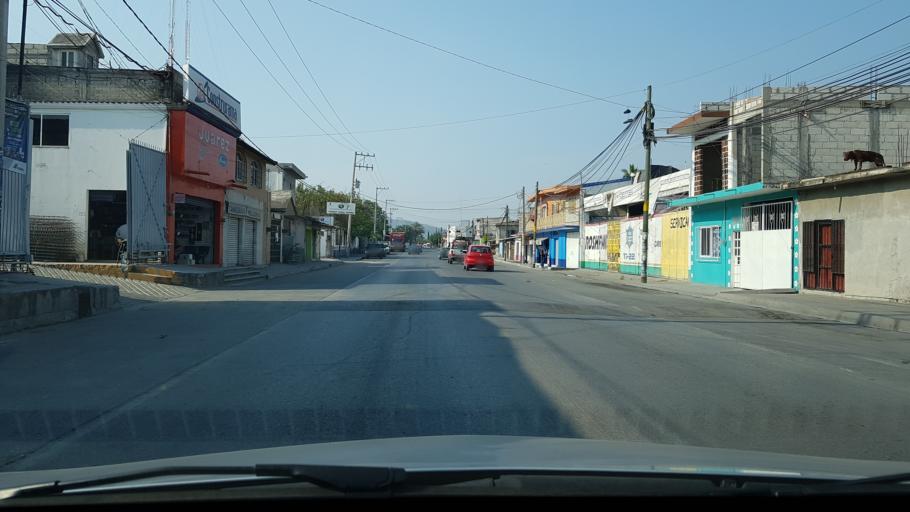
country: MX
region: Morelos
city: Tlaquiltenango
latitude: 18.6447
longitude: -99.1566
